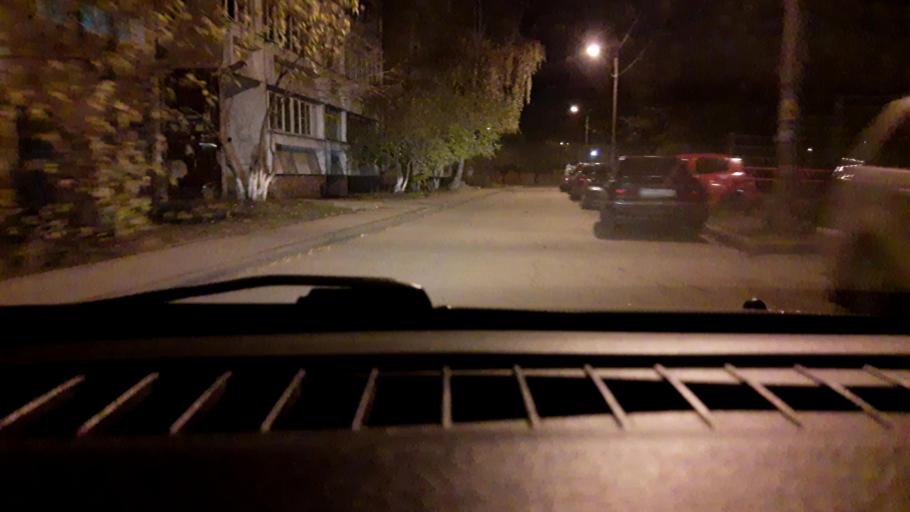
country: RU
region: Nizjnij Novgorod
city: Gorbatovka
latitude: 56.3708
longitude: 43.8018
